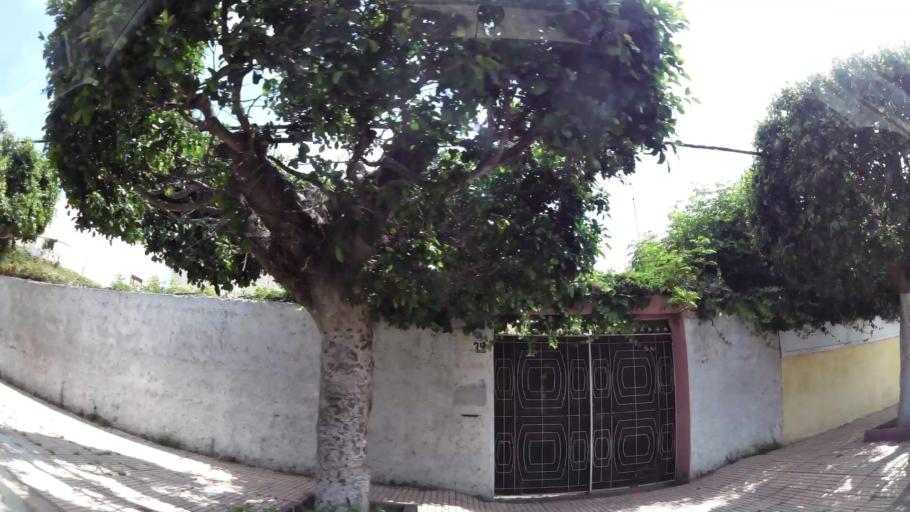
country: MA
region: Rabat-Sale-Zemmour-Zaer
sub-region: Rabat
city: Rabat
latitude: 34.0117
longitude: -6.8462
